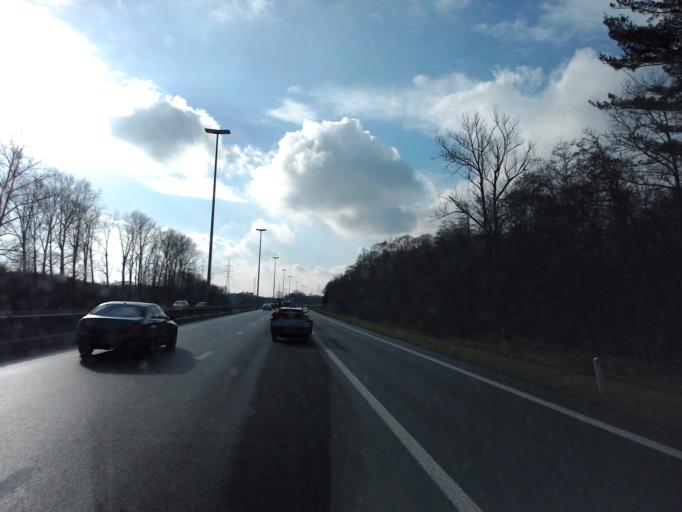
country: BE
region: Flanders
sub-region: Provincie Antwerpen
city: Zandhoven
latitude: 51.2201
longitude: 4.6422
